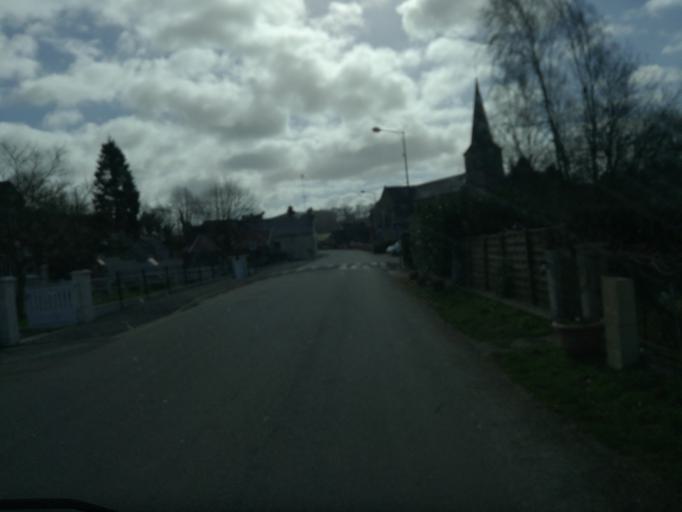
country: FR
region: Haute-Normandie
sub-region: Departement de la Seine-Maritime
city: Bretteville-du-Grand-Caux
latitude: 49.6956
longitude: 0.4761
